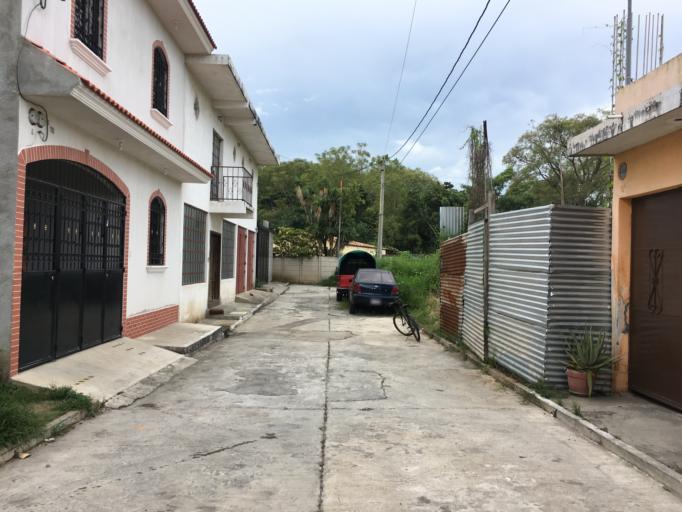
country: GT
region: Guatemala
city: Petapa
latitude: 14.5006
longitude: -90.5652
